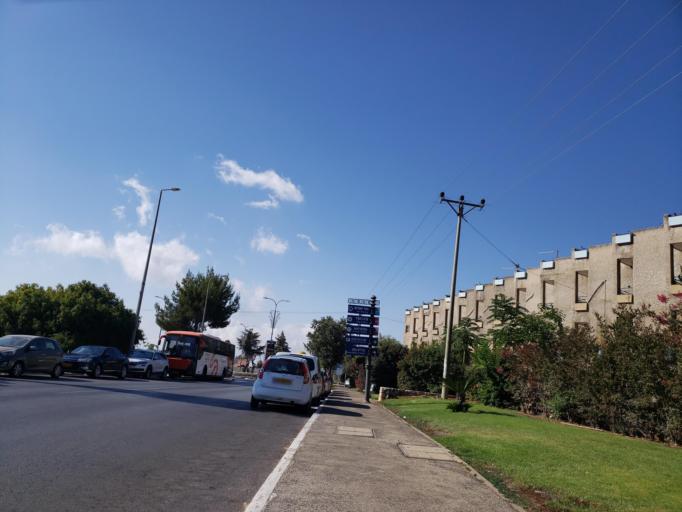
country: IL
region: Northern District
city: Safed
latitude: 32.9644
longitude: 35.4981
